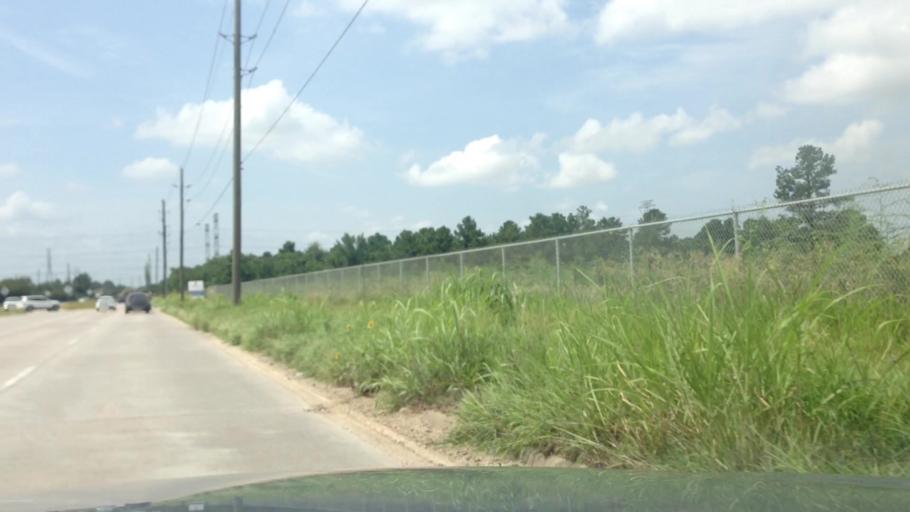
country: US
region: Texas
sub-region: Harris County
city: Jersey Village
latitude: 29.9427
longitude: -95.5469
